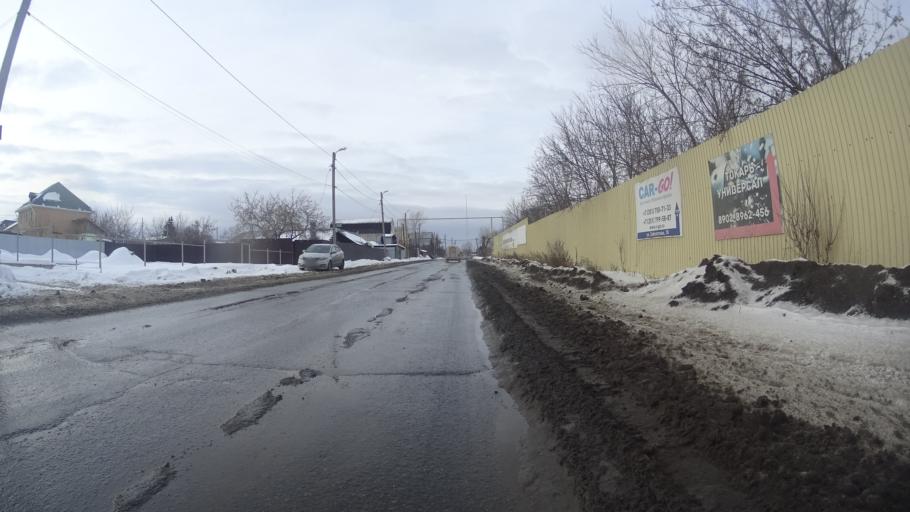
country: RU
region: Chelyabinsk
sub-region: Gorod Chelyabinsk
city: Chelyabinsk
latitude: 55.1291
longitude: 61.4002
